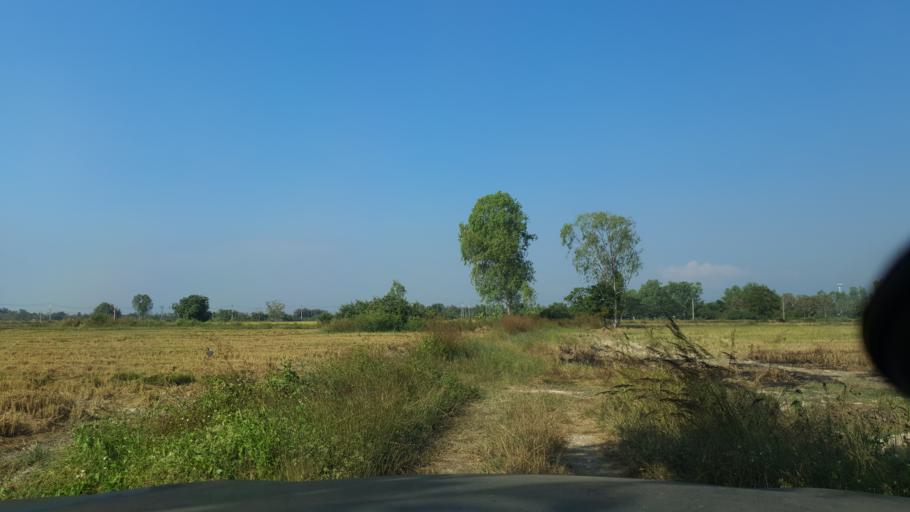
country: TH
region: Lamphun
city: Ban Thi
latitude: 18.6765
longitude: 99.1331
